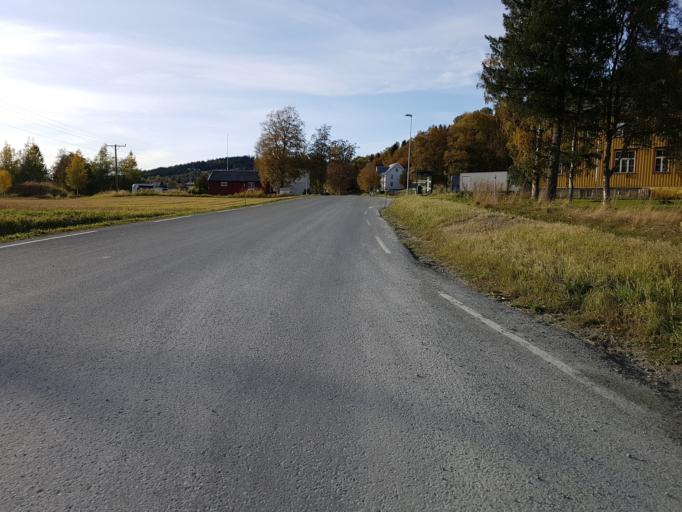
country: NO
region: Sor-Trondelag
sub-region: Klaebu
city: Klaebu
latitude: 63.3494
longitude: 10.4985
